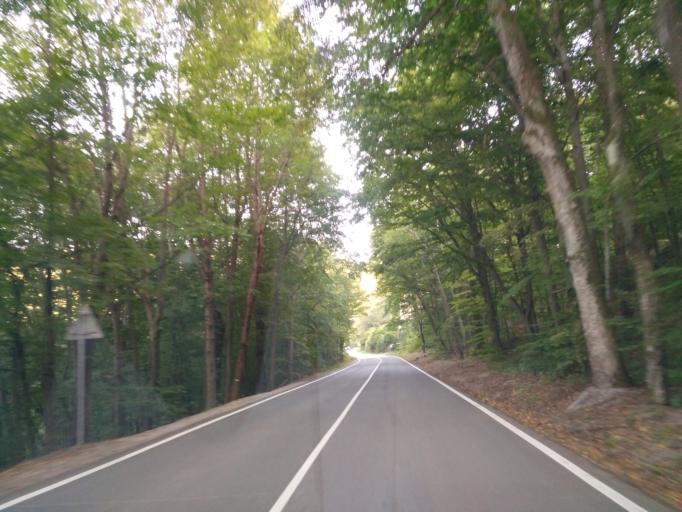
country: SK
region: Kosicky
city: Kosice
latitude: 48.7481
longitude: 21.2044
